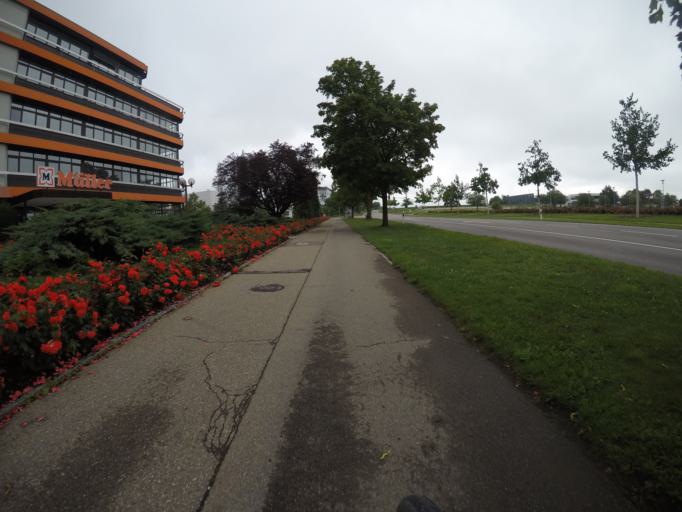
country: DE
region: Baden-Wuerttemberg
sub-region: Tuebingen Region
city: Ulm
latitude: 48.4280
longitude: 9.9855
